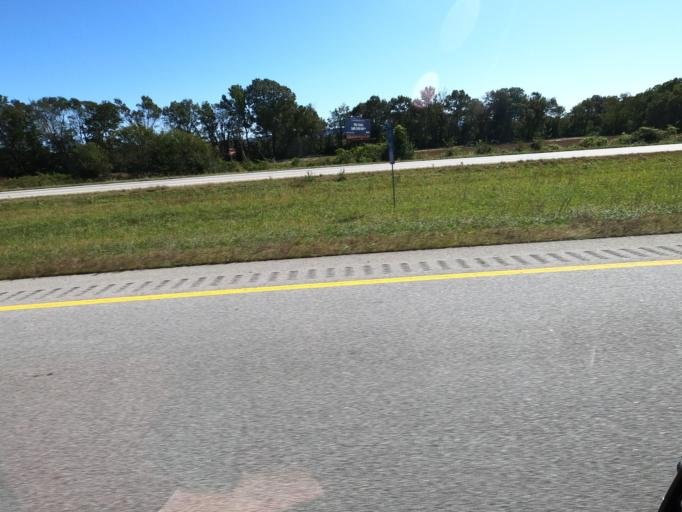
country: US
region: Tennessee
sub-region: Marion County
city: Kimball
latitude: 35.0422
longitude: -85.6756
